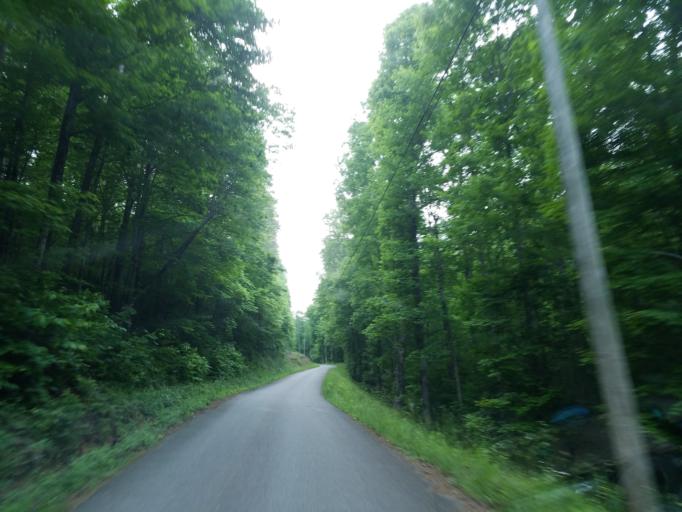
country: US
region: Georgia
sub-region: Lumpkin County
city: Dahlonega
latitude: 34.5941
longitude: -84.0801
